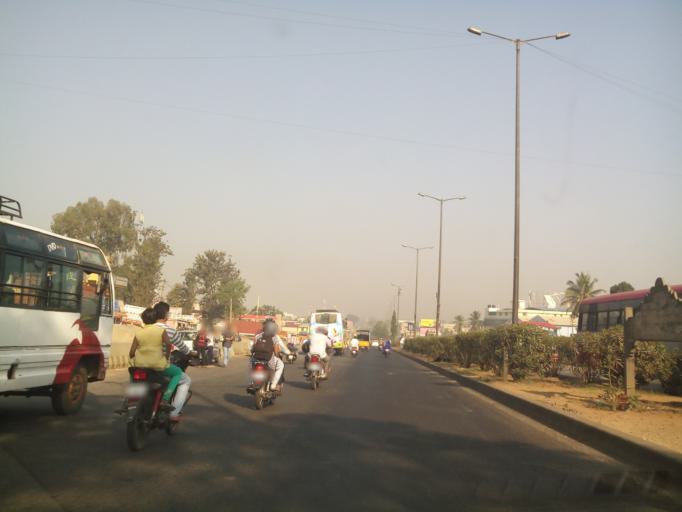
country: IN
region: Karnataka
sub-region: Bangalore Rural
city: Nelamangala
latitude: 13.0609
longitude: 77.4614
